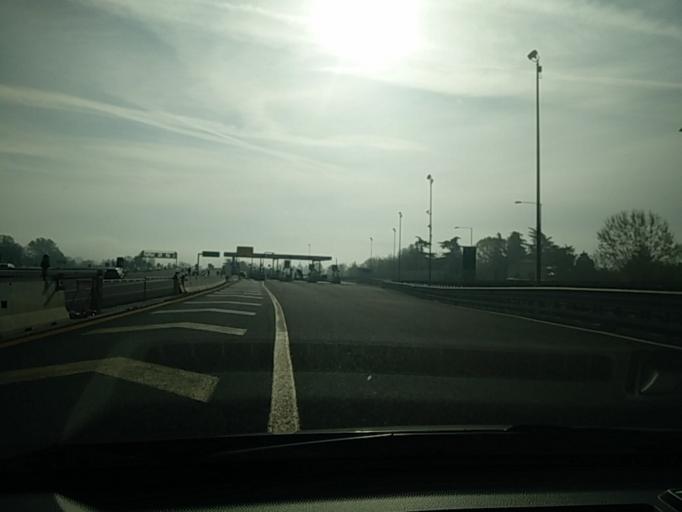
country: IT
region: Emilia-Romagna
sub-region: Provincia di Bologna
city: San Lazzaro
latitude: 44.4804
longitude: 11.4242
